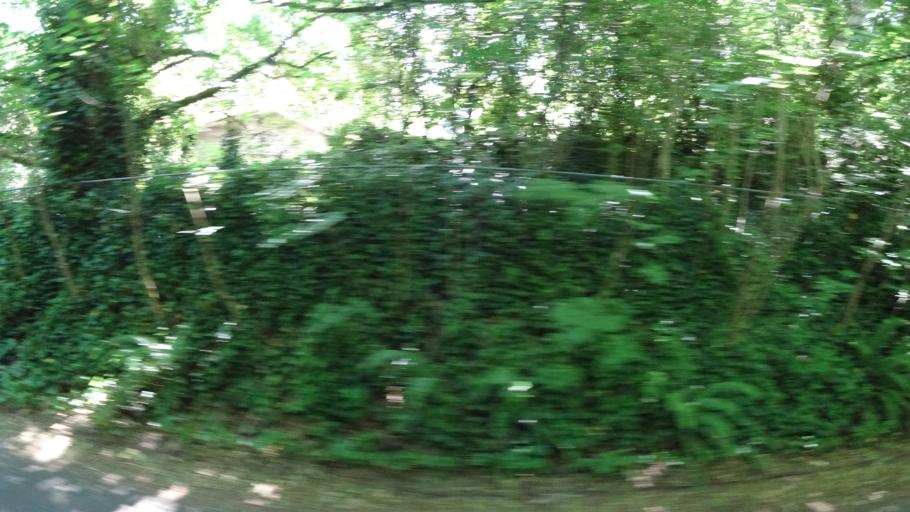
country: US
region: Oregon
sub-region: Clackamas County
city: Lake Oswego
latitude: 45.4358
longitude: -122.6966
